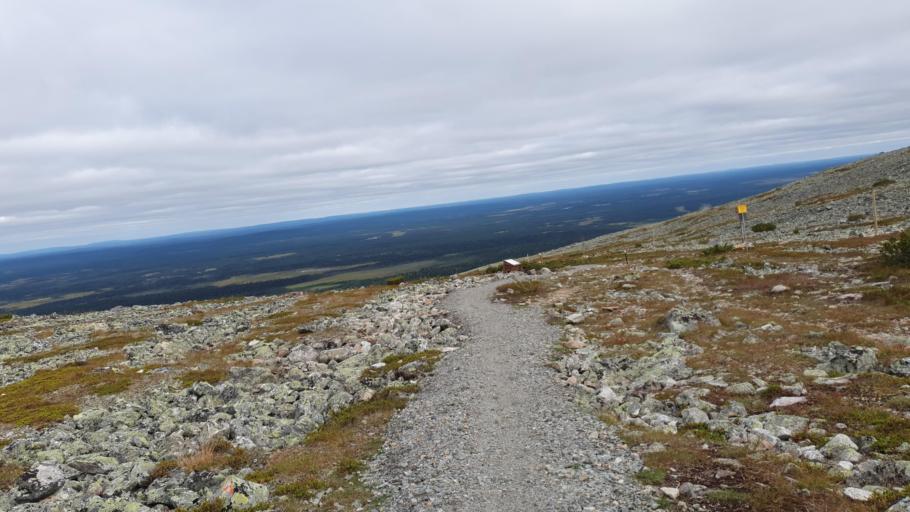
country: FI
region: Lapland
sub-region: Tunturi-Lappi
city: Kolari
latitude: 67.5688
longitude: 24.2359
